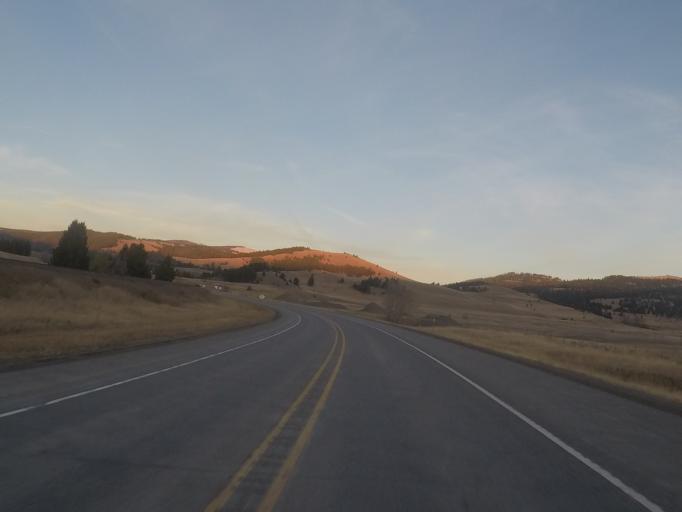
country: US
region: Montana
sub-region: Lewis and Clark County
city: Helena West Side
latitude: 46.5568
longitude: -112.3973
